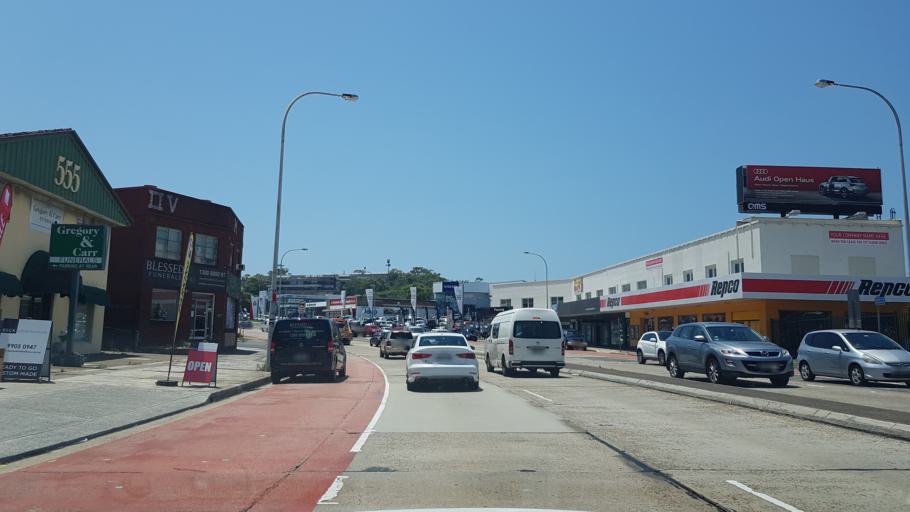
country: AU
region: New South Wales
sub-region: Warringah
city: Brookvale
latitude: -33.7612
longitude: 151.2764
